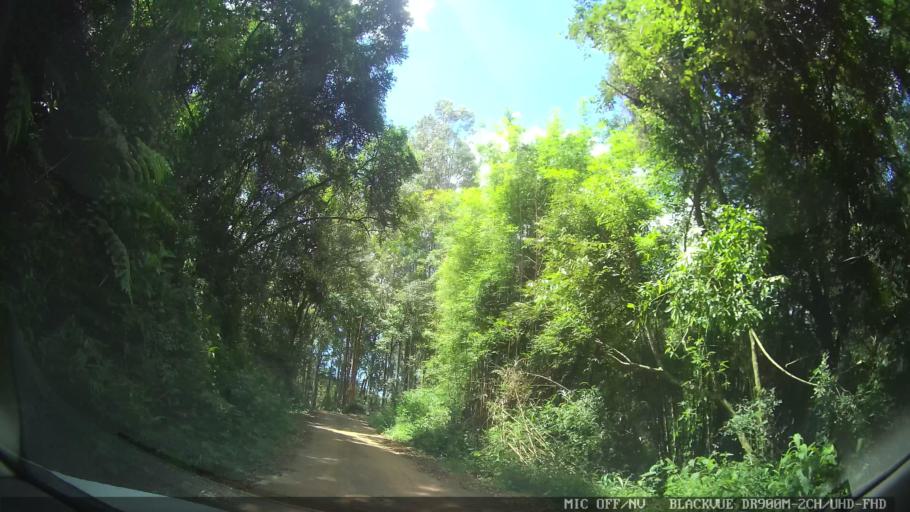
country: BR
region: Minas Gerais
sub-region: Extrema
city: Extrema
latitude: -22.8771
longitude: -46.2939
